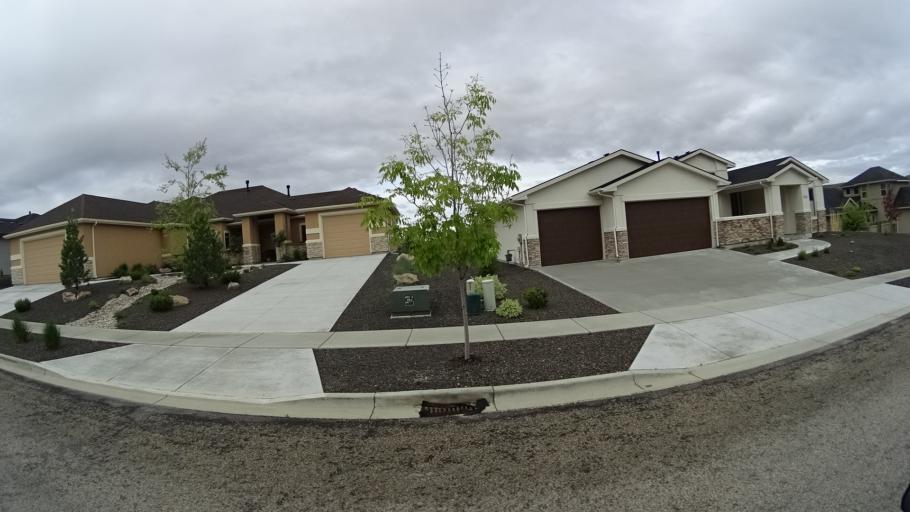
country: US
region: Idaho
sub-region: Ada County
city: Eagle
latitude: 43.7714
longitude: -116.2557
